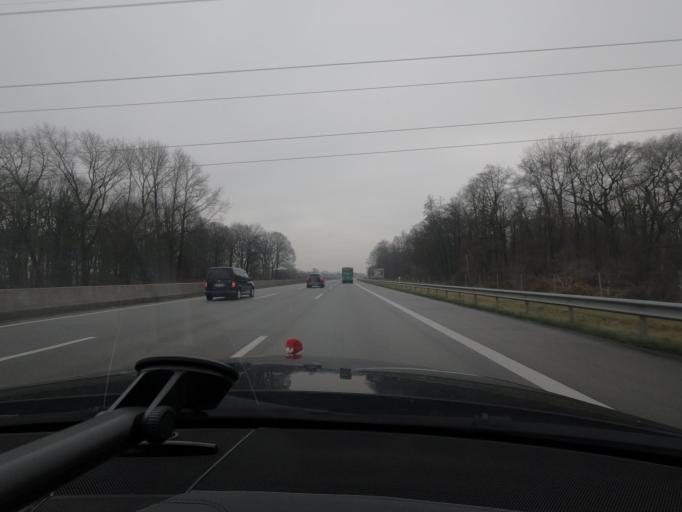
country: DE
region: Schleswig-Holstein
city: Norderstedt
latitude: 53.6869
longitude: 9.9456
